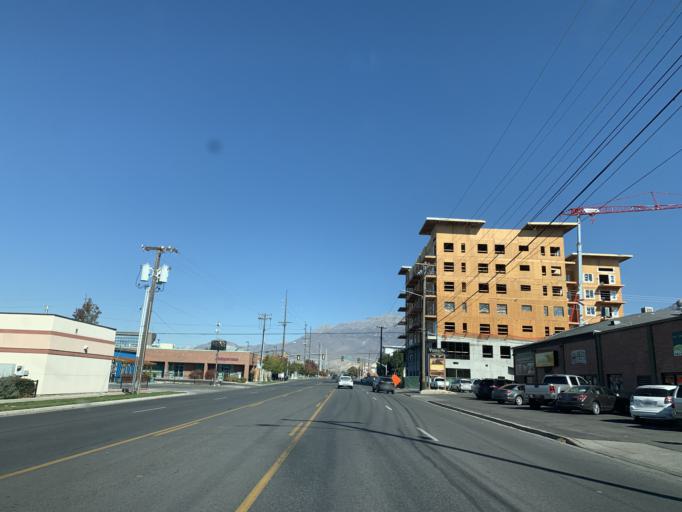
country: US
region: Utah
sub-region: Utah County
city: Provo
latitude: 40.2393
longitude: -111.6621
